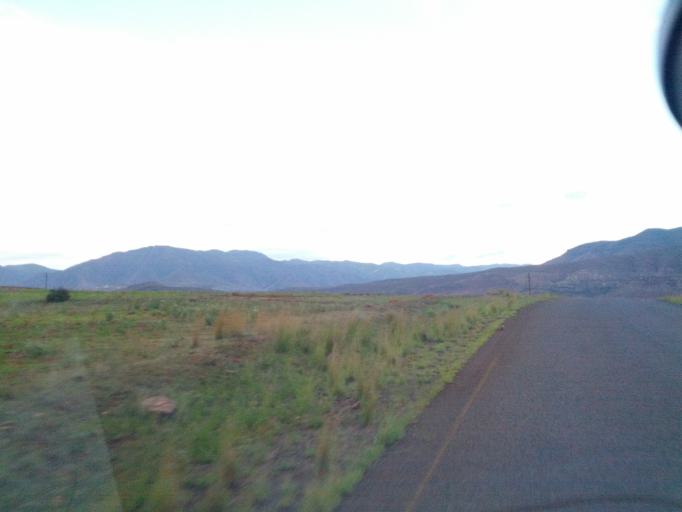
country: LS
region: Qacha's Nek
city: Qacha's Nek
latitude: -30.0597
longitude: 28.3796
